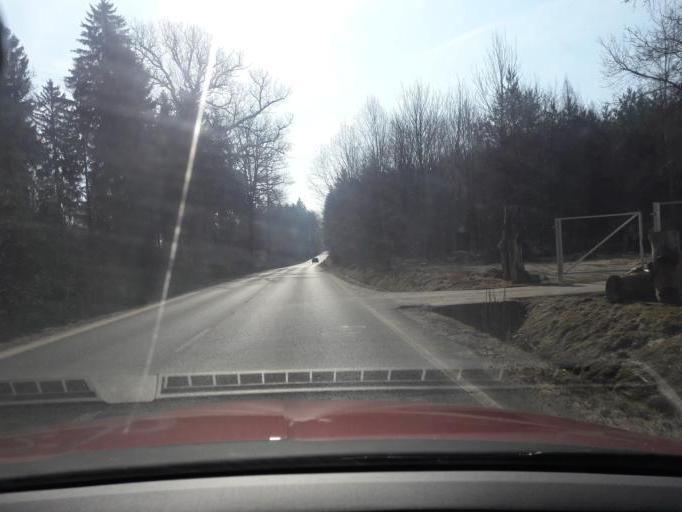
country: CZ
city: Novy Bor
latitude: 50.7529
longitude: 14.5656
